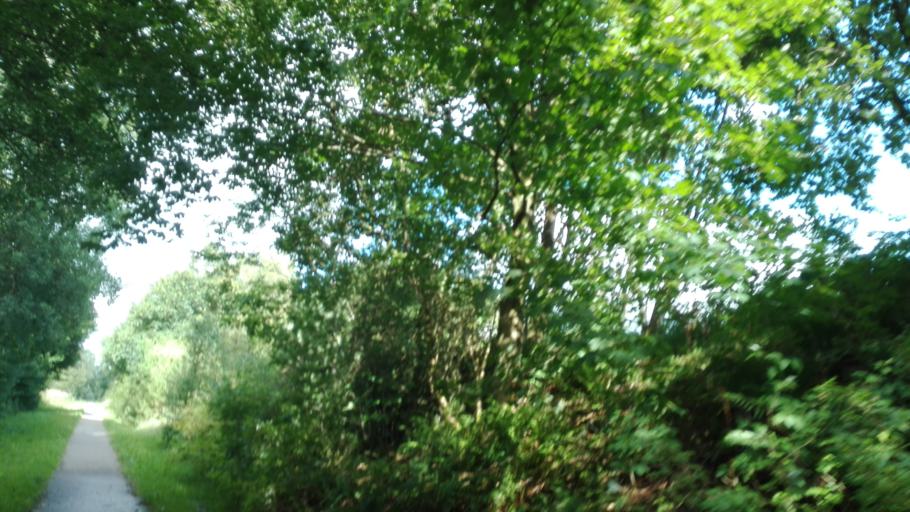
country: DK
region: Central Jutland
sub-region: Silkeborg Kommune
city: Virklund
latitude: 56.0658
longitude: 9.4925
